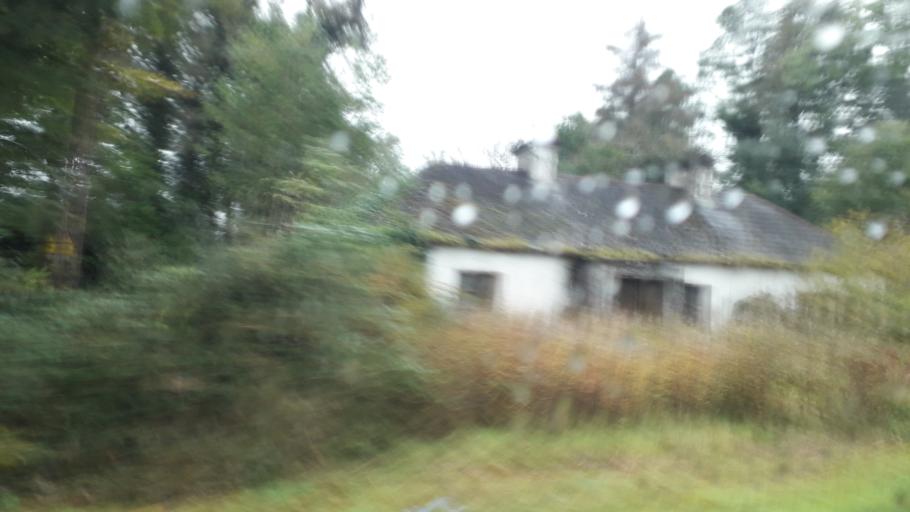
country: IE
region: Connaught
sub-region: Roscommon
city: Roscommon
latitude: 53.7880
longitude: -8.2695
